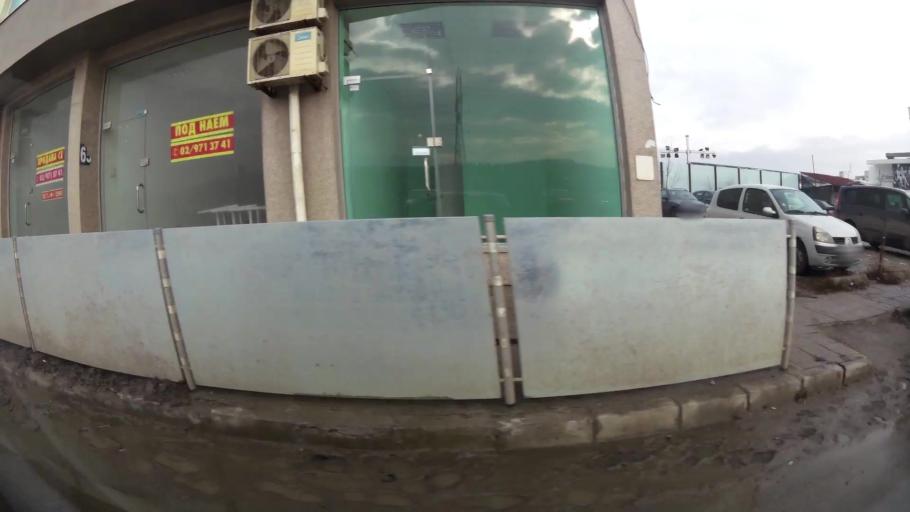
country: BG
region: Sofia-Capital
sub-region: Stolichna Obshtina
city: Sofia
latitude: 42.7091
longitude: 23.2565
